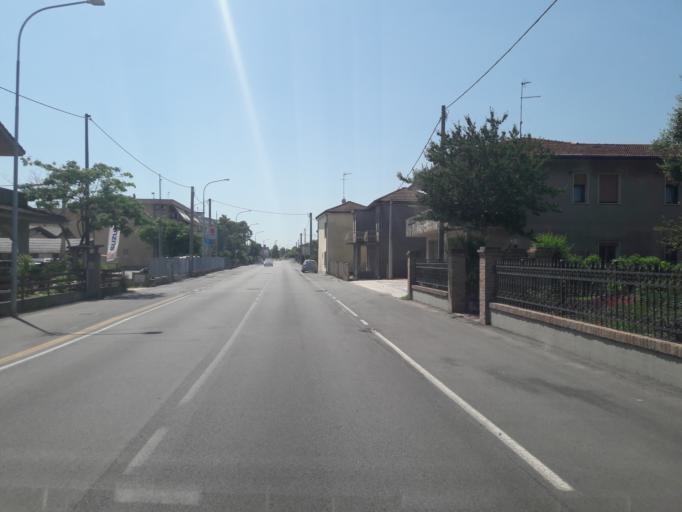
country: IT
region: Veneto
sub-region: Provincia di Rovigo
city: Taglio di Po
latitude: 45.0006
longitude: 12.2104
